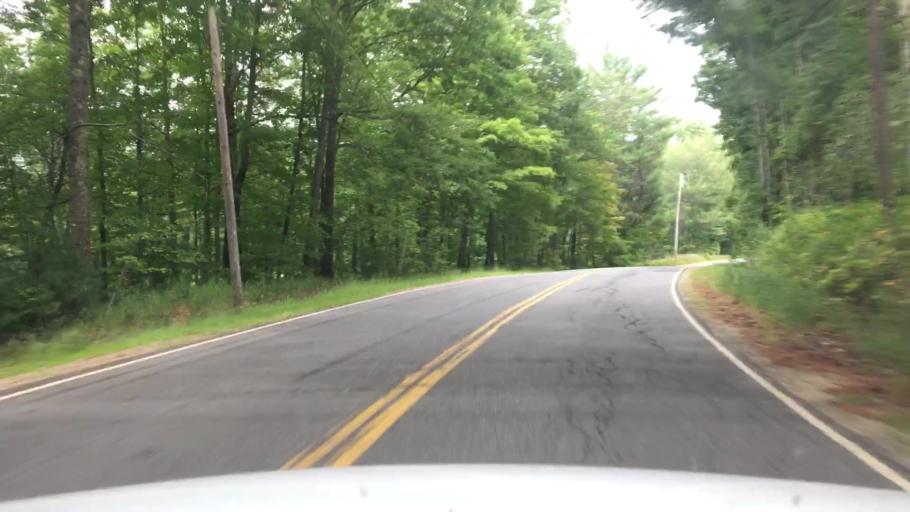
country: US
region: Maine
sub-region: Oxford County
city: Rumford
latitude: 44.5464
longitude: -70.6902
